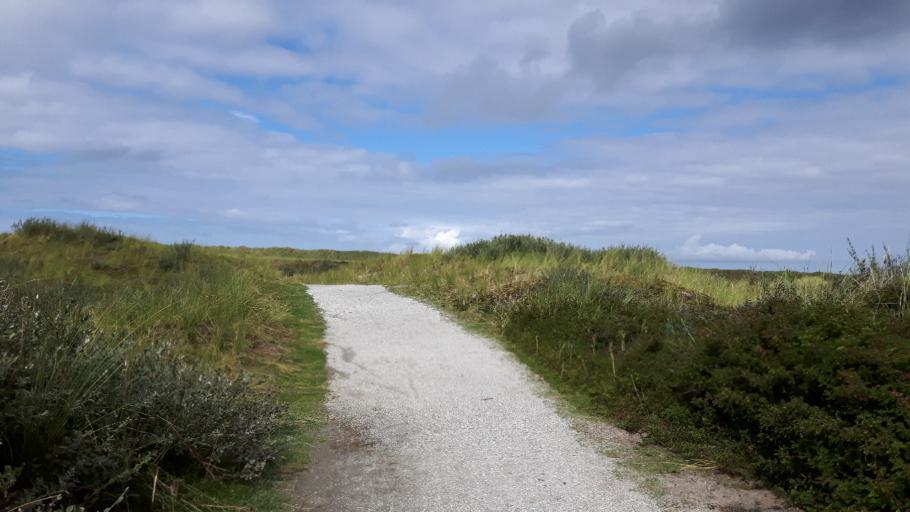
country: NL
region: Friesland
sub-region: Gemeente Ameland
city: Hollum
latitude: 53.4521
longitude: 5.6206
